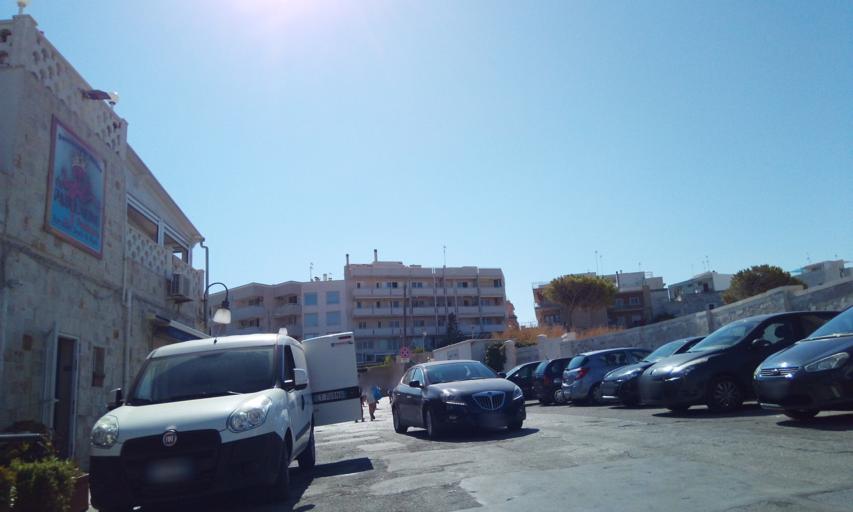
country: IT
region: Apulia
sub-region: Provincia di Bari
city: Polignano a Mare
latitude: 40.9984
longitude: 17.2143
